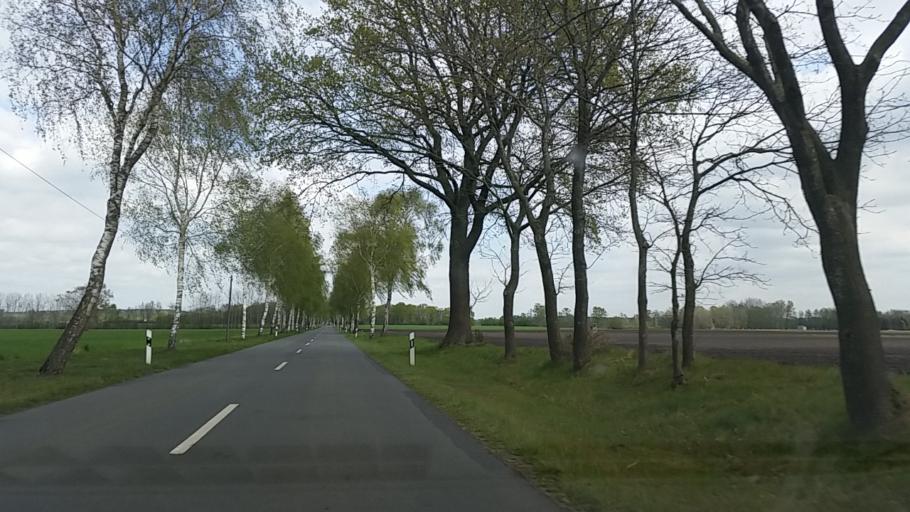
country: DE
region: Lower Saxony
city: Konigsmoor
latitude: 53.2071
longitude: 9.7095
